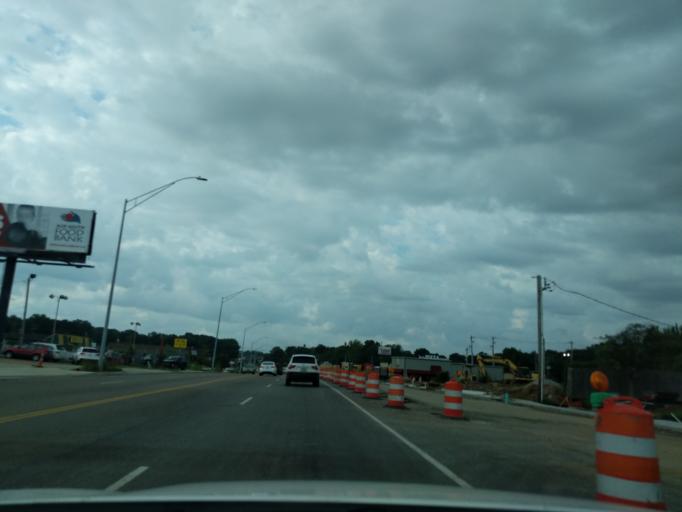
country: US
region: Tennessee
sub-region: Shelby County
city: New South Memphis
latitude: 35.0577
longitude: -90.0245
